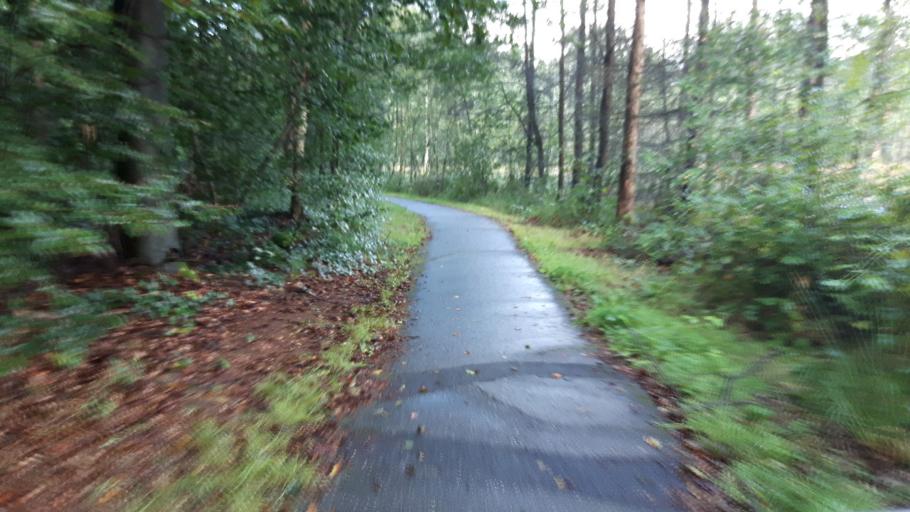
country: NL
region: Friesland
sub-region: Gemeente Smallingerland
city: Drachten
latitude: 53.0678
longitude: 6.1103
